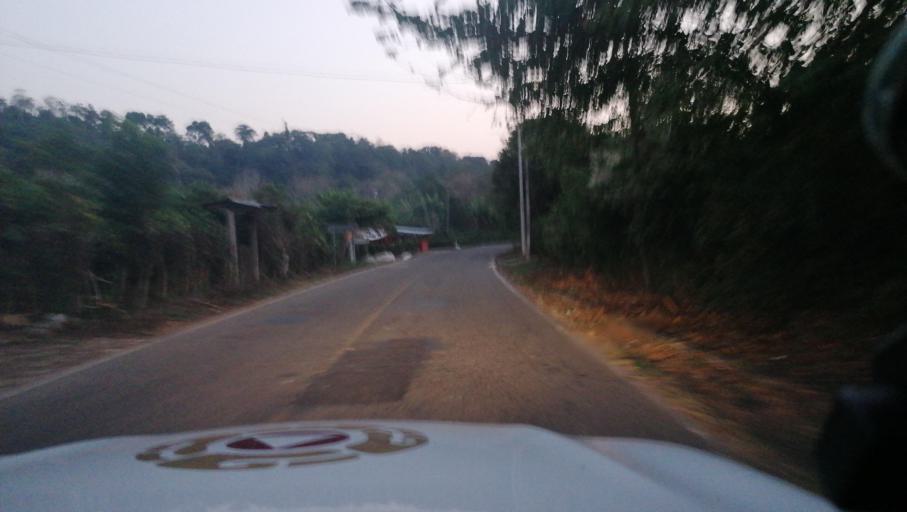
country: MX
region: Chiapas
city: Veinte de Noviembre
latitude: 14.9843
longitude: -92.2423
